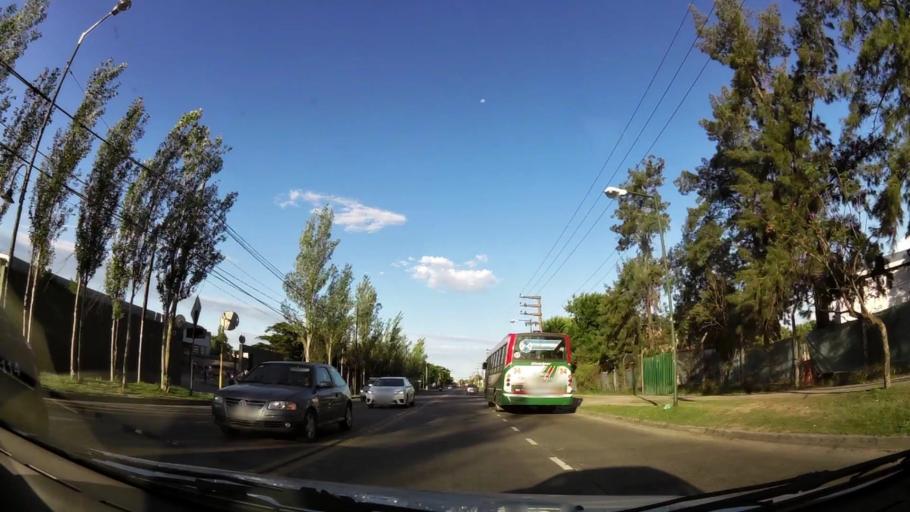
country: AR
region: Buenos Aires
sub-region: Partido de San Isidro
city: San Isidro
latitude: -34.4644
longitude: -58.5520
